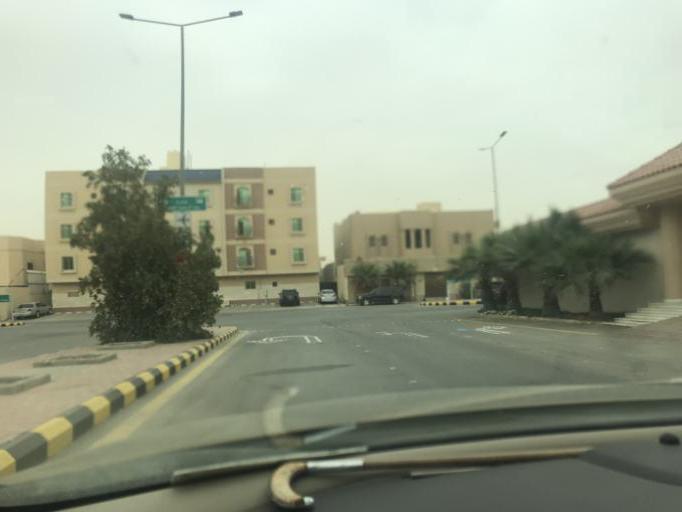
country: SA
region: Ar Riyad
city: Riyadh
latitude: 24.7376
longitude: 46.7557
